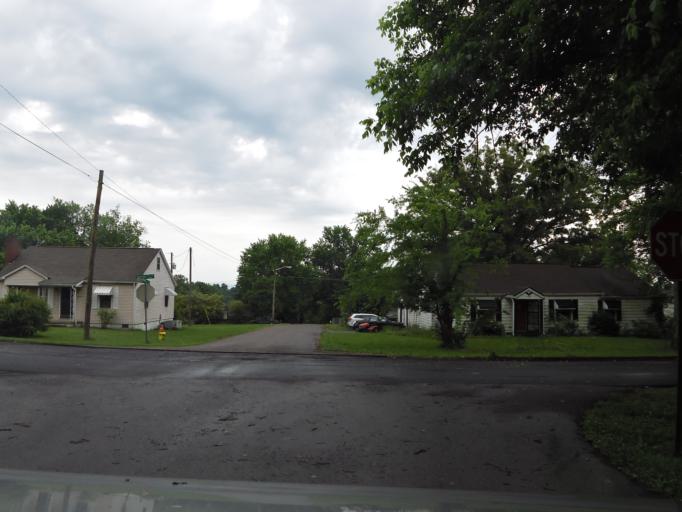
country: US
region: Tennessee
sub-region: Knox County
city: Knoxville
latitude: 36.0001
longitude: -83.9028
